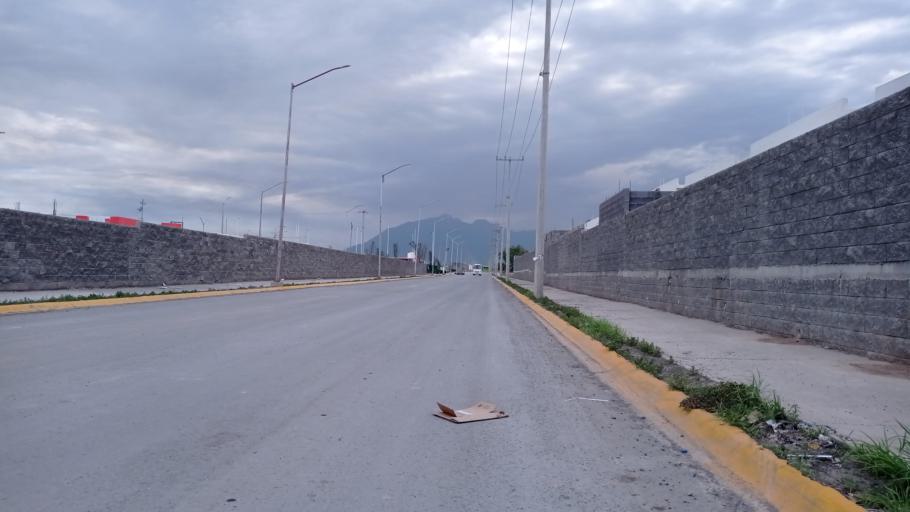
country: MX
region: Nuevo Leon
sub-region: Salinas Victoria
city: Simeprodeso (Colectivo Nuevo)
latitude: 25.8770
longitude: -100.3177
